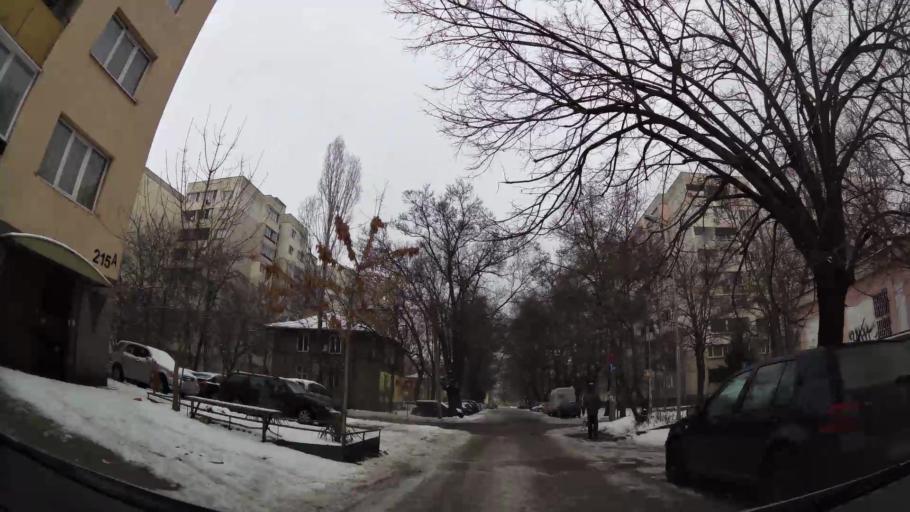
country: BG
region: Sofia-Capital
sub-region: Stolichna Obshtina
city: Sofia
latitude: 42.7128
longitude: 23.3023
